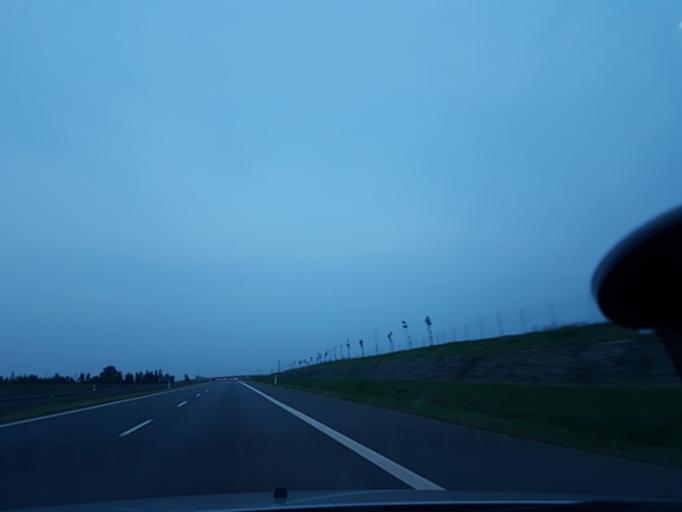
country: PL
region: Lodz Voivodeship
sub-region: Powiat kutnowski
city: Krzyzanow
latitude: 52.1641
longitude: 19.4836
